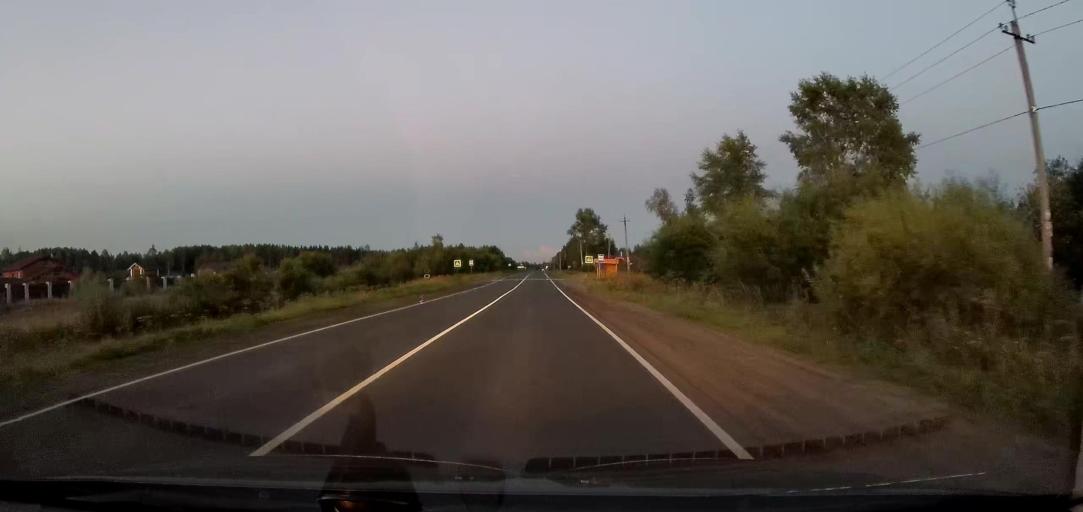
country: RU
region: Arkhangelskaya
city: Uyemskiy
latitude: 64.4468
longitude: 40.9474
